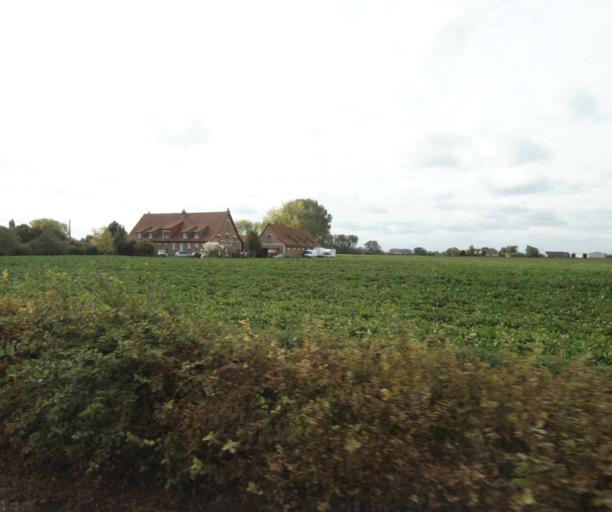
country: FR
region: Nord-Pas-de-Calais
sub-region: Departement du Nord
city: Bois-Grenier
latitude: 50.6539
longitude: 2.8735
